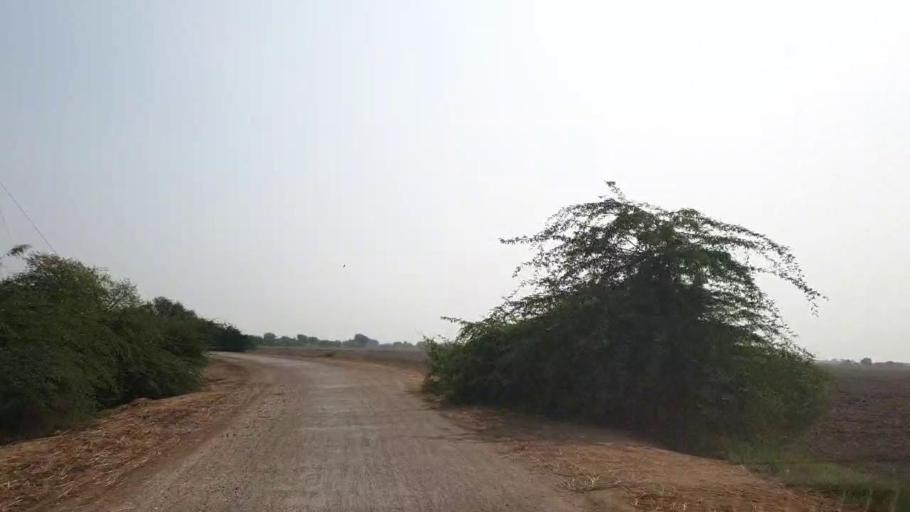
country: PK
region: Sindh
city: Matli
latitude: 24.9908
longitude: 68.5782
